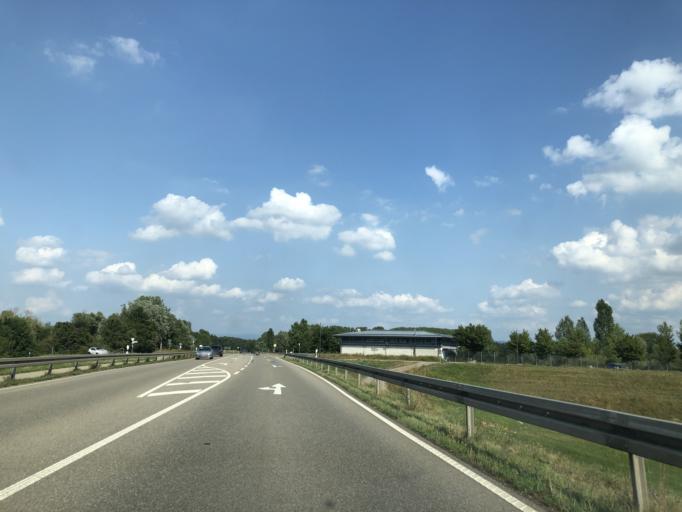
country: FR
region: Alsace
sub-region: Departement du Bas-Rhin
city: Plobsheim
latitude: 48.4942
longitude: 7.7932
